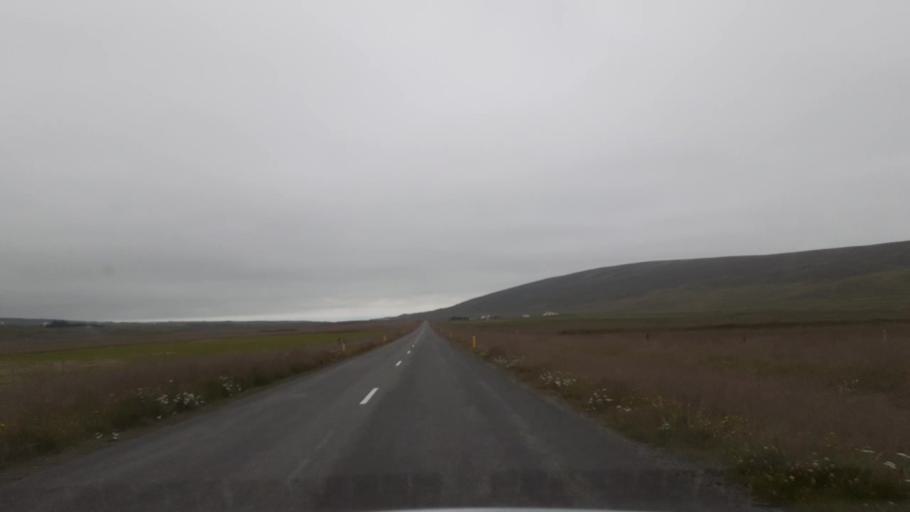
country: IS
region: Northeast
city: Siglufjoerdur
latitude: 65.7426
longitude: -19.1481
